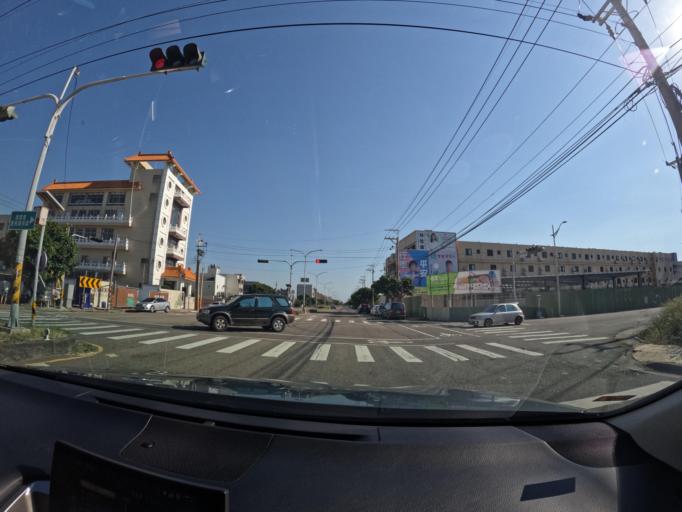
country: TW
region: Taiwan
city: Fengyuan
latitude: 24.2572
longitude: 120.5526
